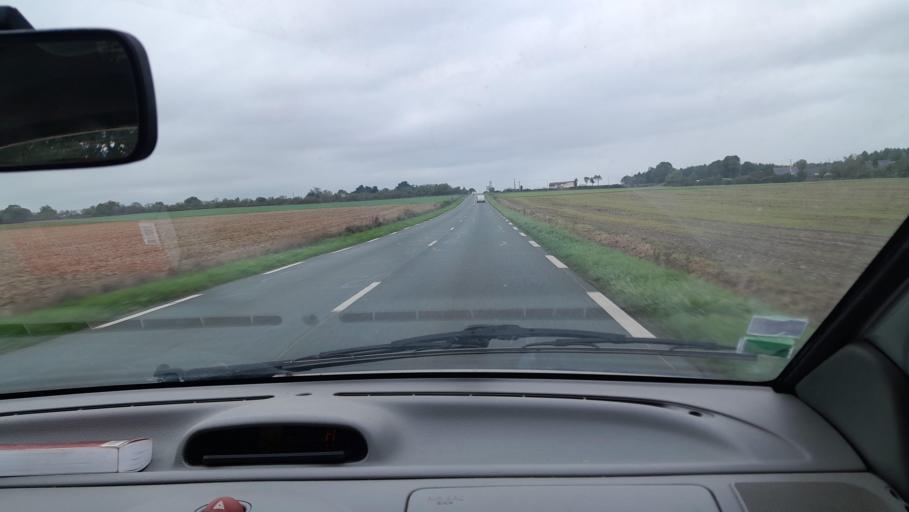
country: FR
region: Pays de la Loire
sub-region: Departement de la Loire-Atlantique
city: Saint-Mars-la-Jaille
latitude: 47.5666
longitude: -1.1877
